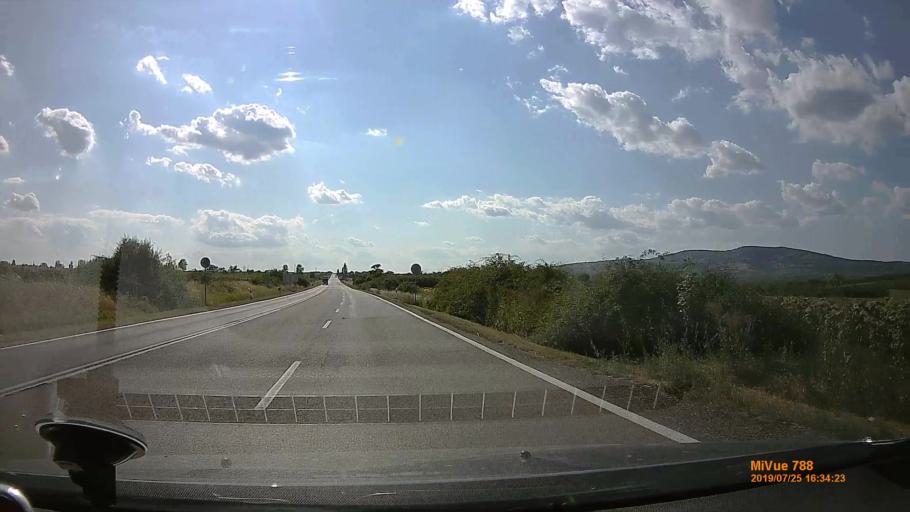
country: HU
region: Heves
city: Abasar
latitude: 47.7669
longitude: 20.0251
